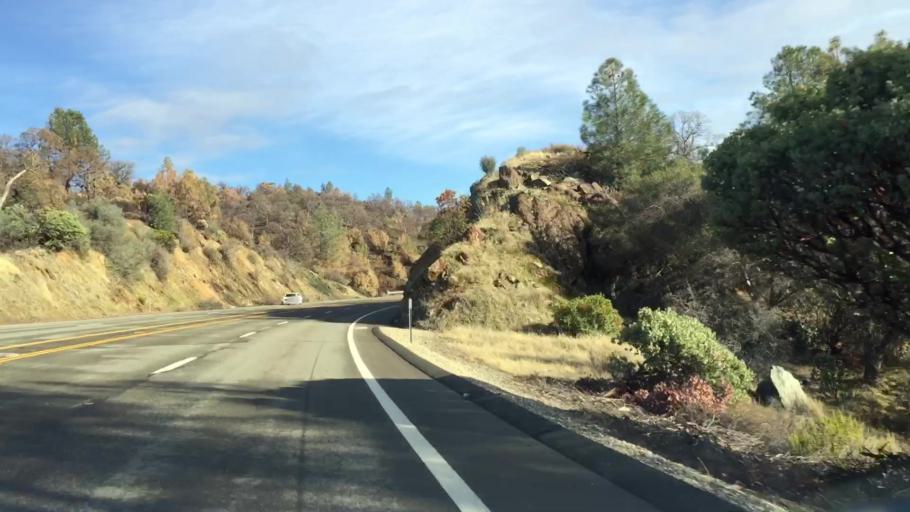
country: US
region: California
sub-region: Butte County
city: Paradise
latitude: 39.6855
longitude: -121.5392
